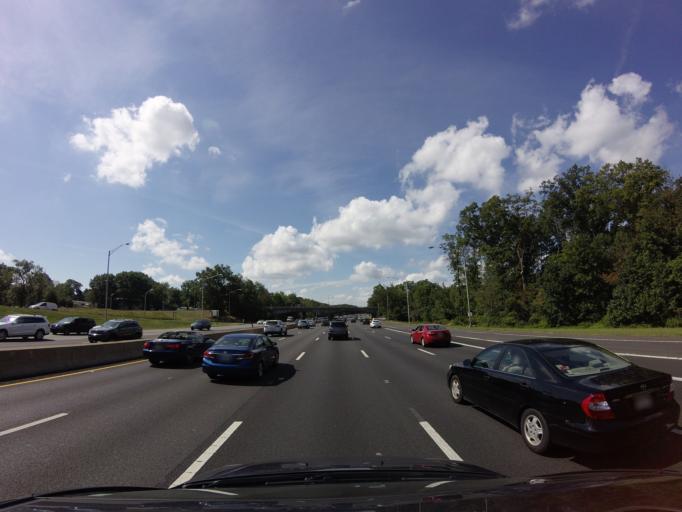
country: US
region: New Jersey
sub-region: Union County
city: Winfield
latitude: 40.6413
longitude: -74.2893
